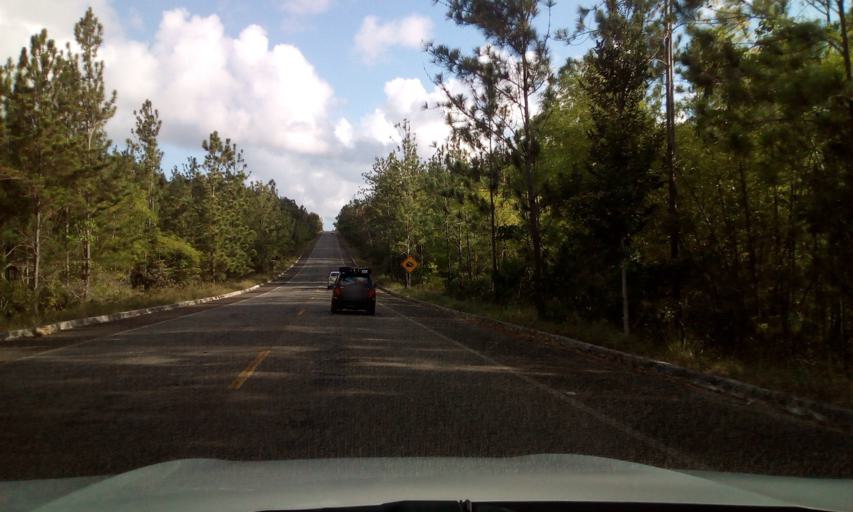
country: BR
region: Bahia
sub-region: Entre Rios
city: Entre Rios
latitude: -12.1274
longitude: -37.7909
